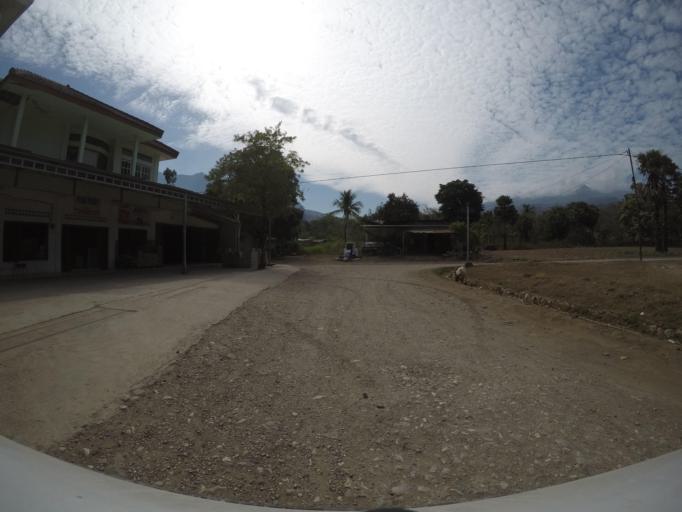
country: TL
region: Bobonaro
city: Maliana
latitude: -8.9910
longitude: 125.2215
